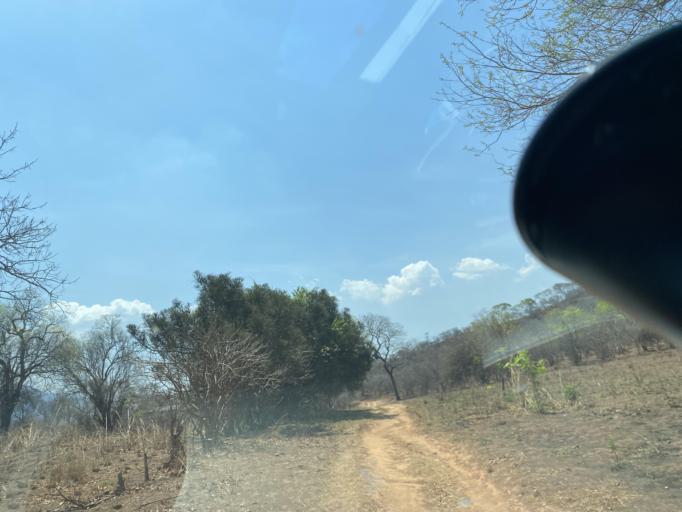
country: ZM
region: Lusaka
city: Kafue
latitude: -15.7816
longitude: 28.4601
